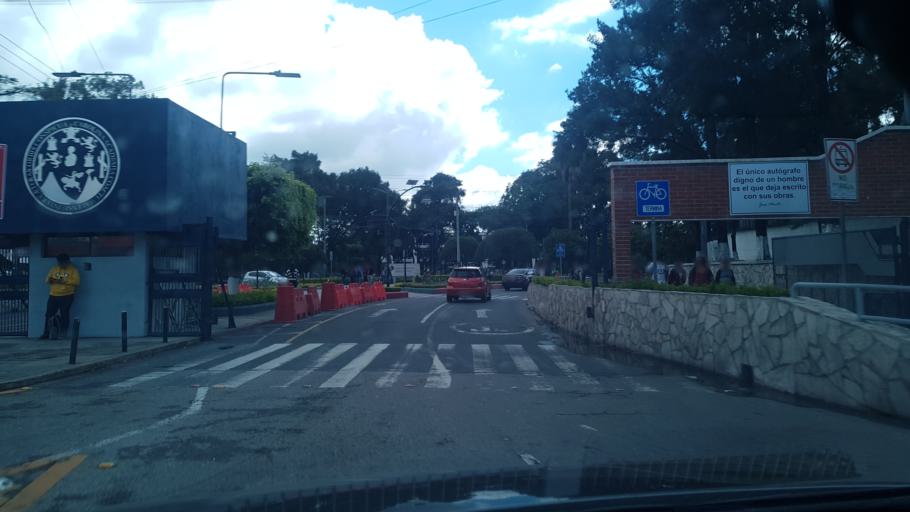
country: GT
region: Guatemala
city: Santa Catarina Pinula
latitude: 14.5900
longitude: -90.5515
